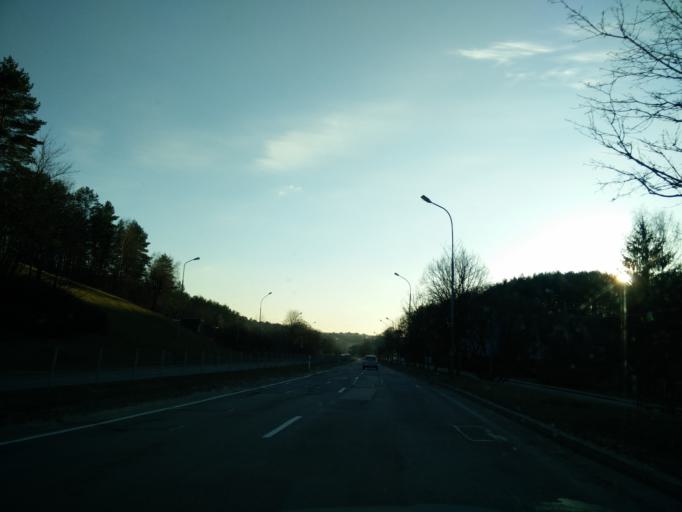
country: LT
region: Vilnius County
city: Rasos
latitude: 54.6885
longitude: 25.3292
